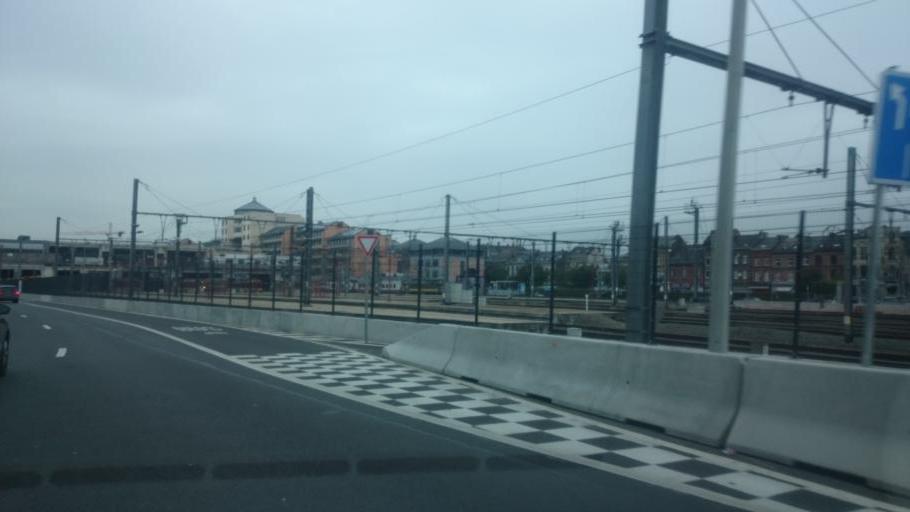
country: BE
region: Wallonia
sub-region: Province de Namur
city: Namur
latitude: 50.4690
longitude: 4.8665
